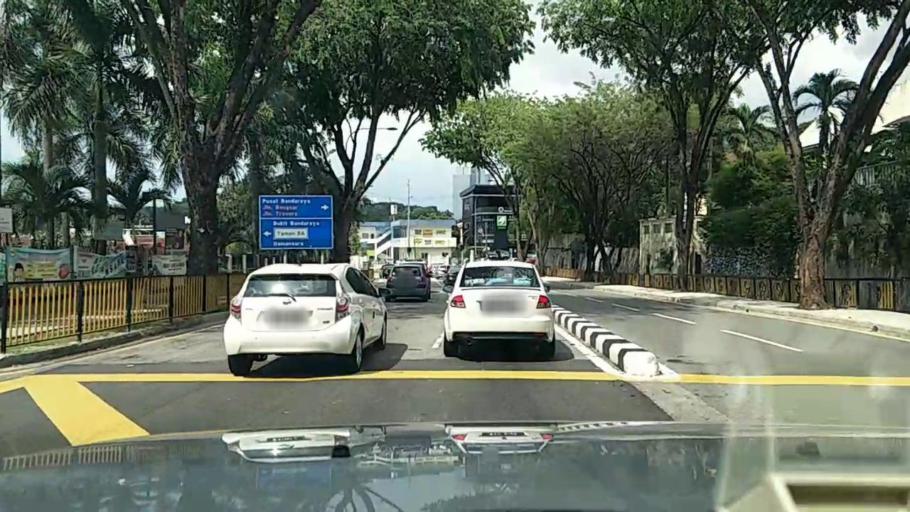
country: MY
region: Kuala Lumpur
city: Kuala Lumpur
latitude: 3.1292
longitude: 101.6721
